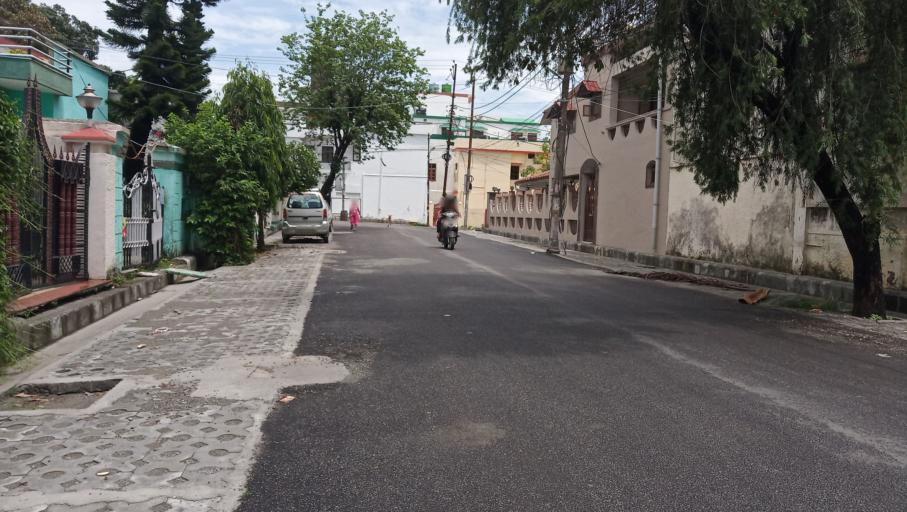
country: IN
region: Uttarakhand
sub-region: Dehradun
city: Dehradun
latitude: 30.3648
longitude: 78.0667
